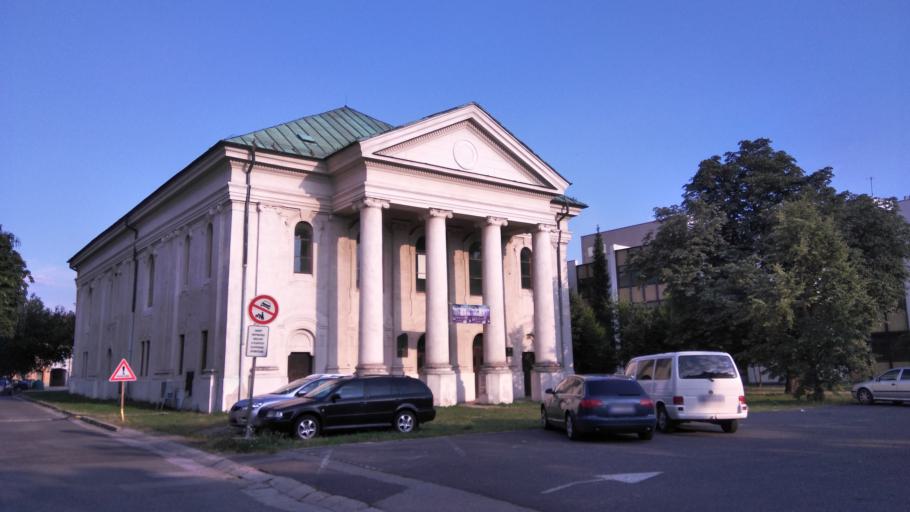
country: SK
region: Zilinsky
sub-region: Okres Liptovsky Mikulas
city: Liptovsky Mikulas
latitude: 49.0849
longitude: 19.6106
